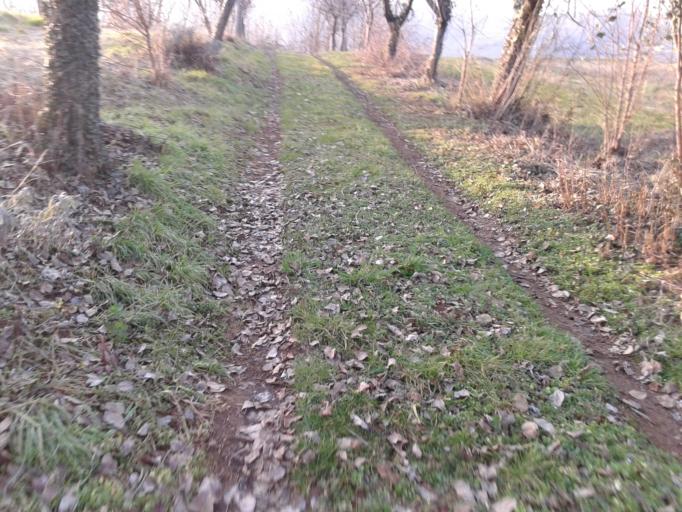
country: IT
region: Veneto
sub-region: Provincia di Vicenza
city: Monte di Malo
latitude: 45.6654
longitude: 11.3658
